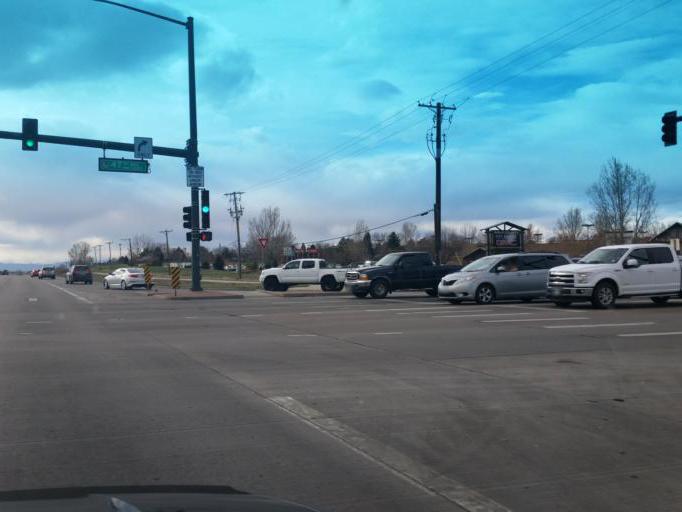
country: US
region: Colorado
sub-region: Weld County
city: Greeley
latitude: 40.3922
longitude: -104.7561
